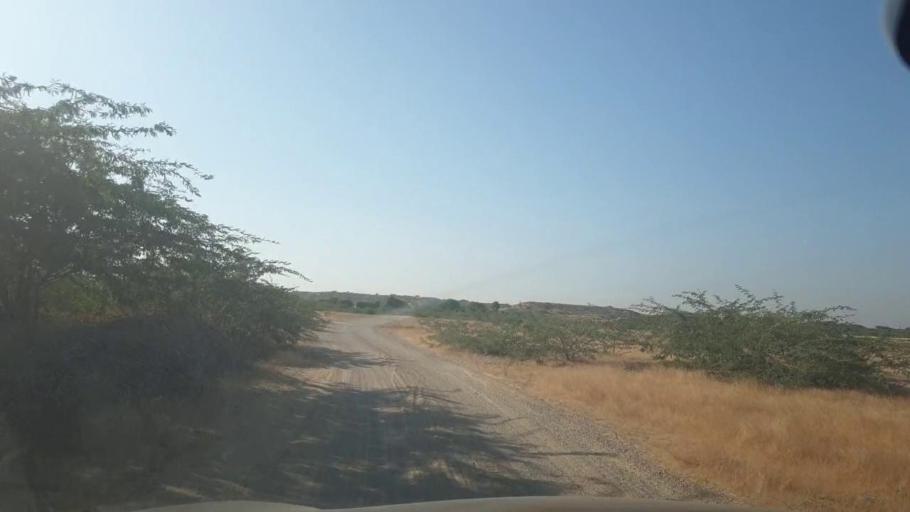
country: PK
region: Sindh
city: Malir Cantonment
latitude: 25.0379
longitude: 67.2608
